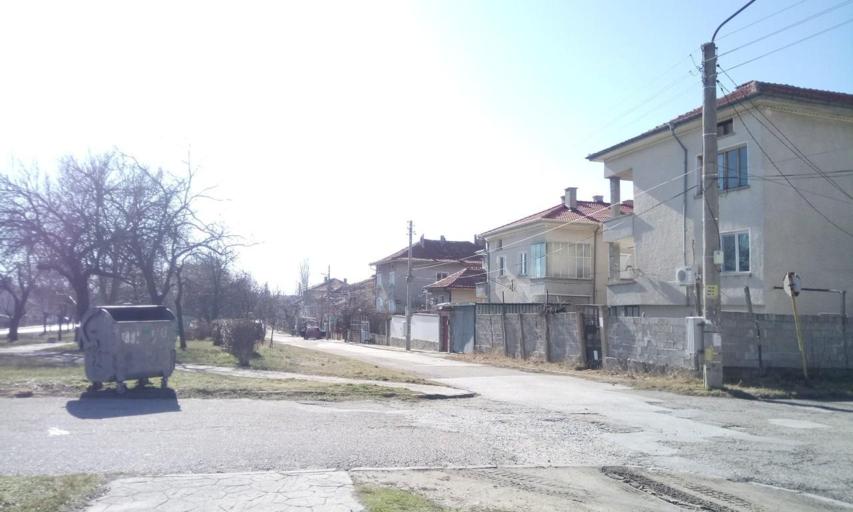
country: BG
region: Plovdiv
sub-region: Obshtina Khisarya
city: Khisarya
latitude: 42.5117
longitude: 24.7155
